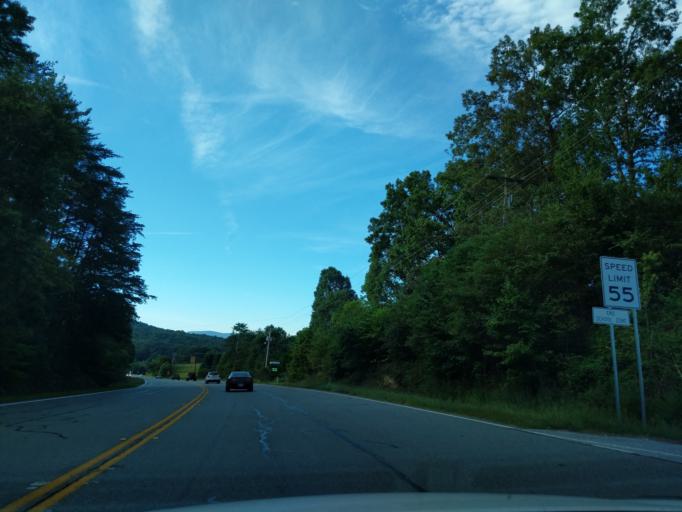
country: US
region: Georgia
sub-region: Fannin County
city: McCaysville
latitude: 34.9198
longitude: -84.3783
